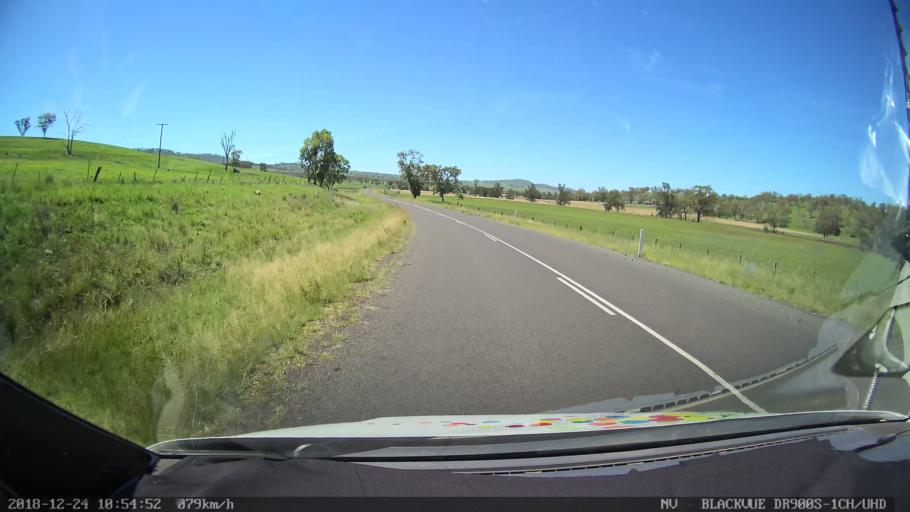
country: AU
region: New South Wales
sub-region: Upper Hunter Shire
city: Merriwa
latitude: -32.0096
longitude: 150.4168
